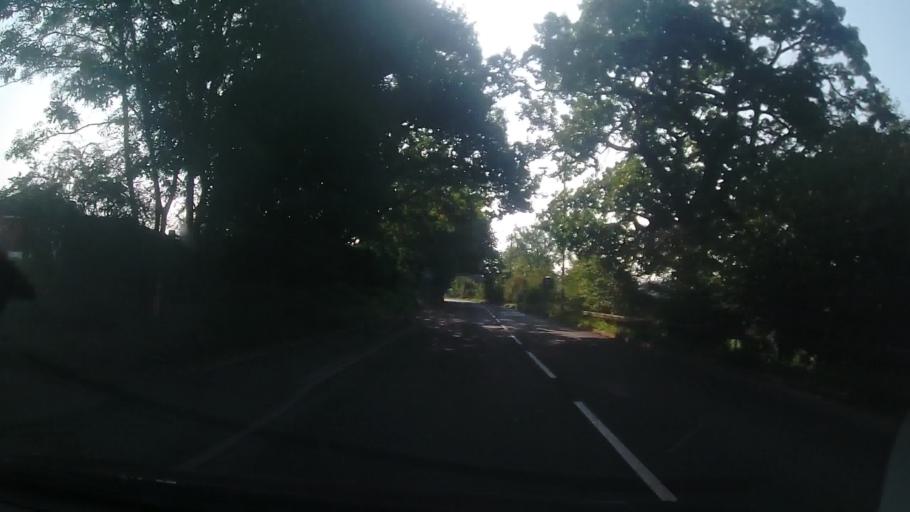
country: GB
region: England
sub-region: Shropshire
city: Bridgnorth
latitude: 52.5257
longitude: -2.4110
